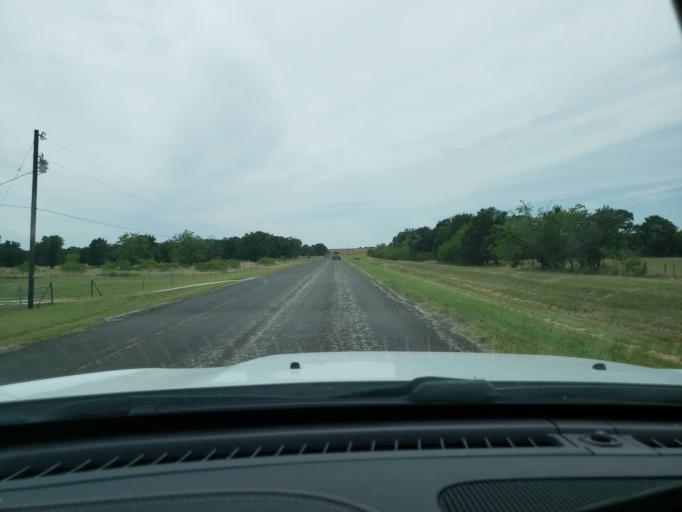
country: US
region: Texas
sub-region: Burleson County
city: Somerville
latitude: 30.3484
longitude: -96.5413
